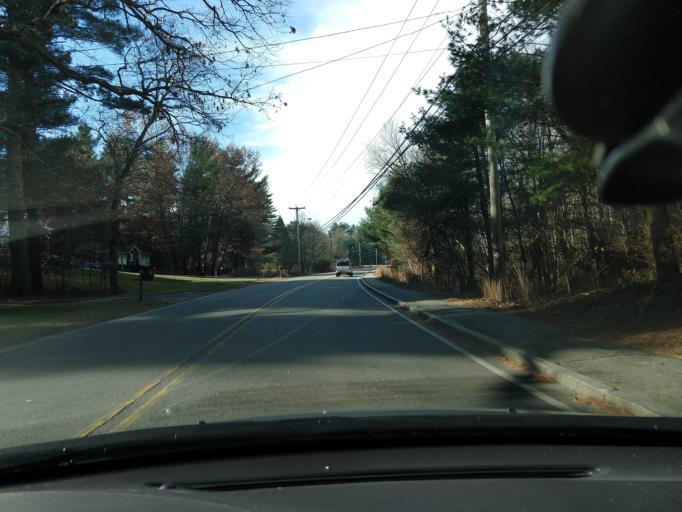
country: US
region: Massachusetts
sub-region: Middlesex County
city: East Pepperell
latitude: 42.6657
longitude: -71.5464
